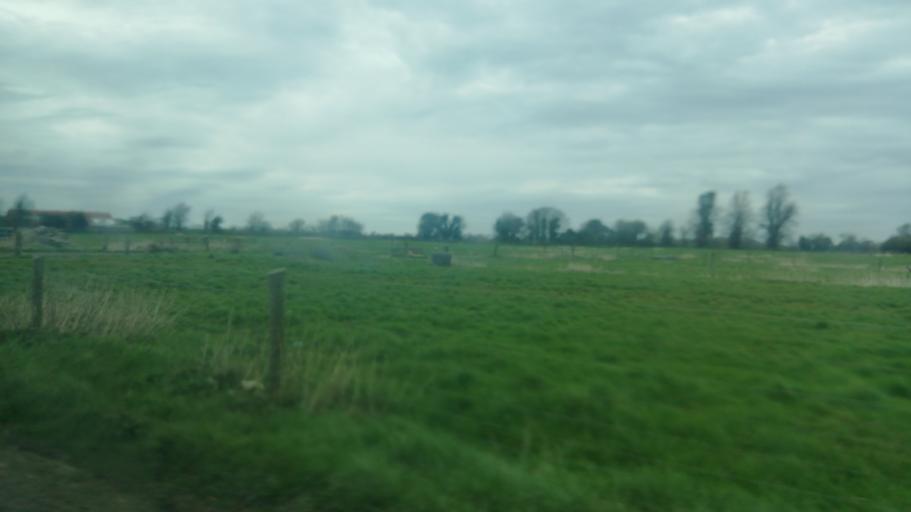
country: IE
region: Leinster
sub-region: Kildare
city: Maynooth
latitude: 53.3530
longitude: -6.6121
